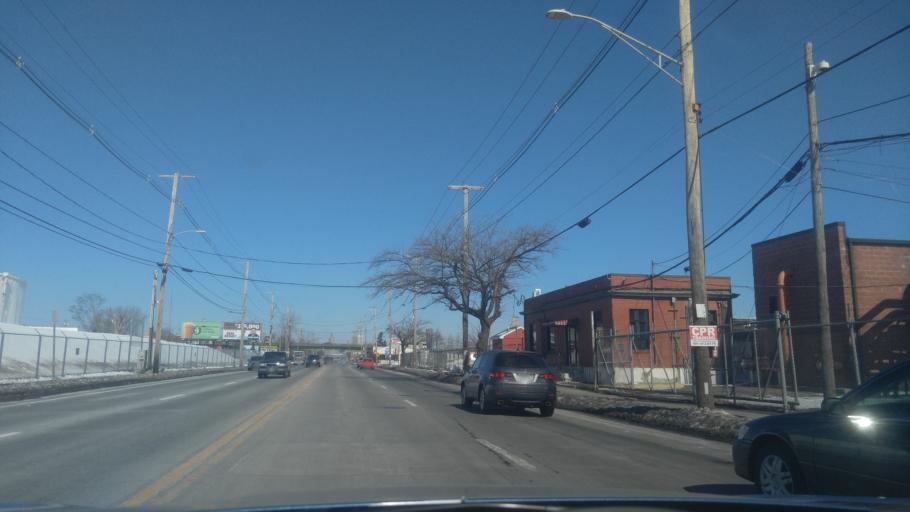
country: US
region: Rhode Island
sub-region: Providence County
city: Providence
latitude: 41.7990
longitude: -71.3996
